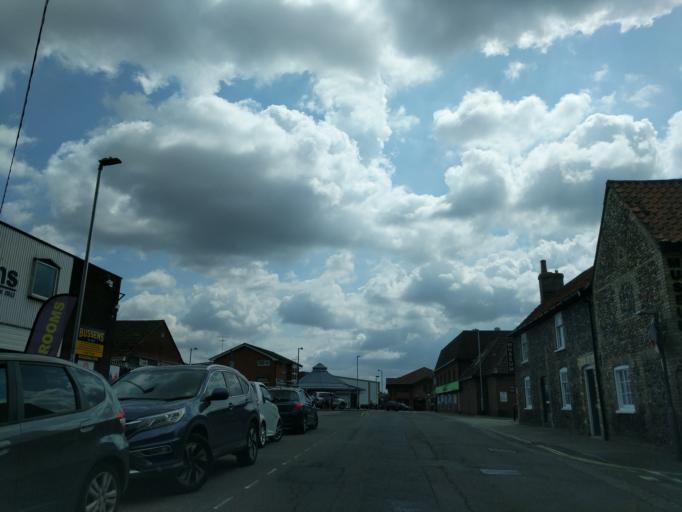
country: GB
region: England
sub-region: Suffolk
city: Lakenheath
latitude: 52.3439
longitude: 0.5116
